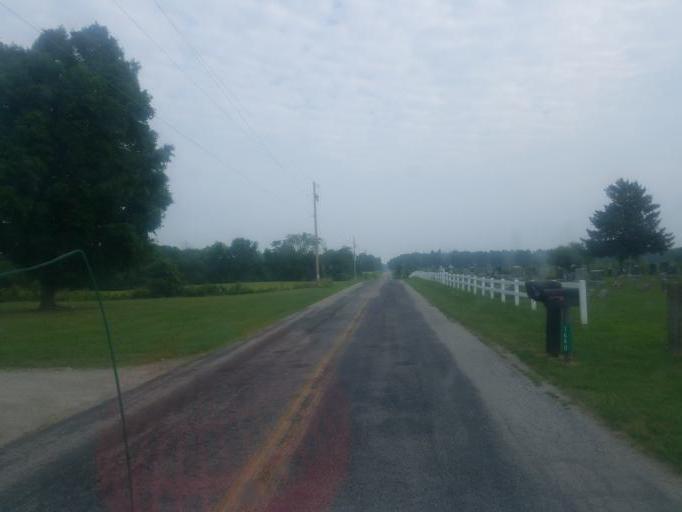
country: US
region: Ohio
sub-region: Morrow County
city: Cardington
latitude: 40.5594
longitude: -82.9766
